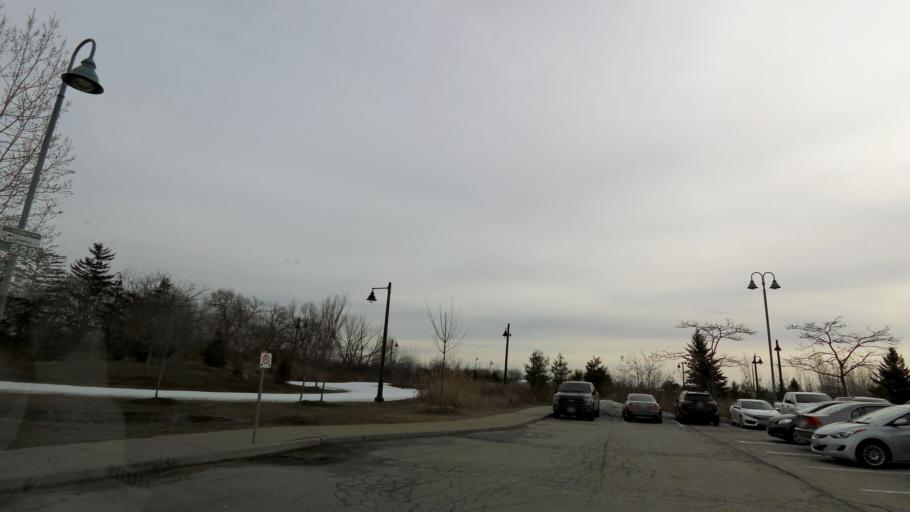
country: CA
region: Ontario
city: Etobicoke
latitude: 43.5932
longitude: -79.5160
